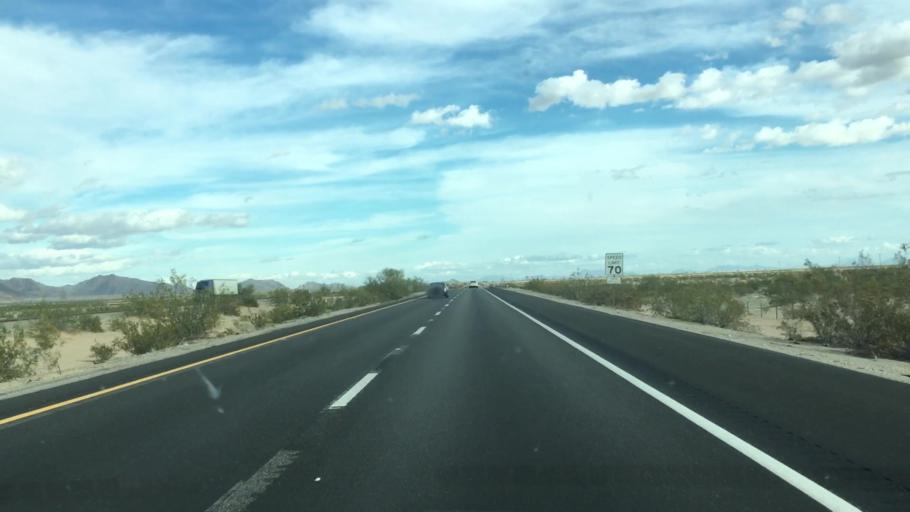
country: US
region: California
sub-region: Riverside County
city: Mesa Verde
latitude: 33.6082
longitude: -114.8847
